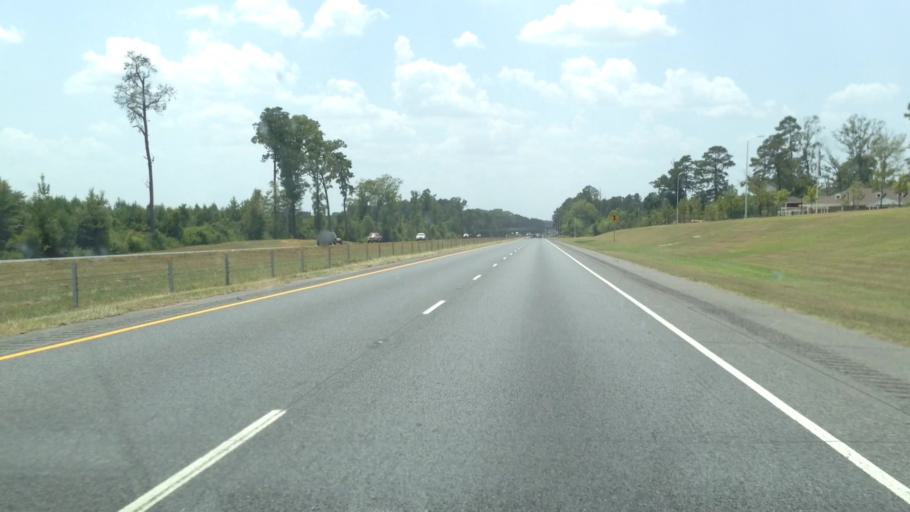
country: US
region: Louisiana
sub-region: Lincoln Parish
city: Ruston
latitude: 32.5288
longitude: -92.4462
